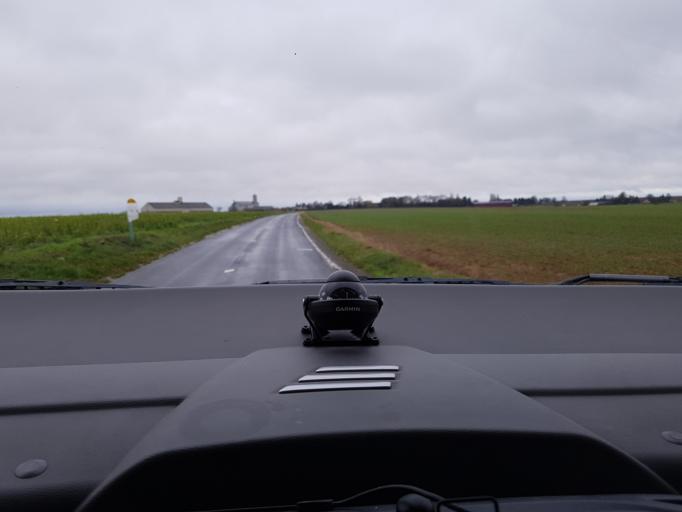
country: FR
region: Haute-Normandie
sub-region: Departement de l'Eure
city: Fleury-sur-Andelle
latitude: 49.2934
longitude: 1.3402
